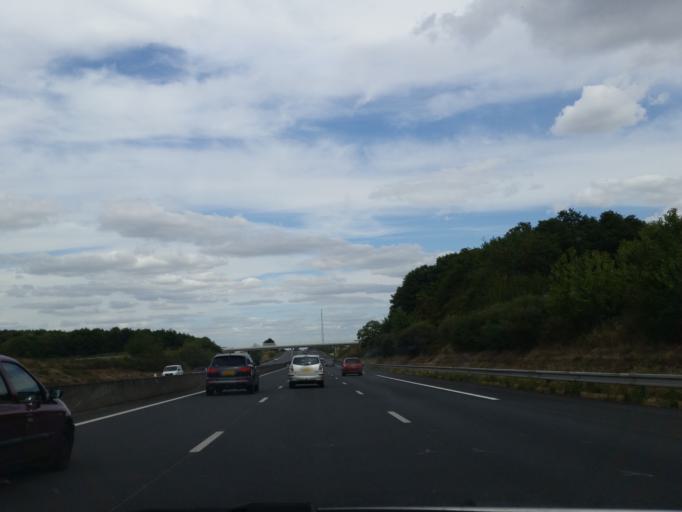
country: FR
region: Centre
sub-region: Departement d'Indre-et-Loire
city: Auzouer-en-Touraine
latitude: 47.5562
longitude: 1.0169
